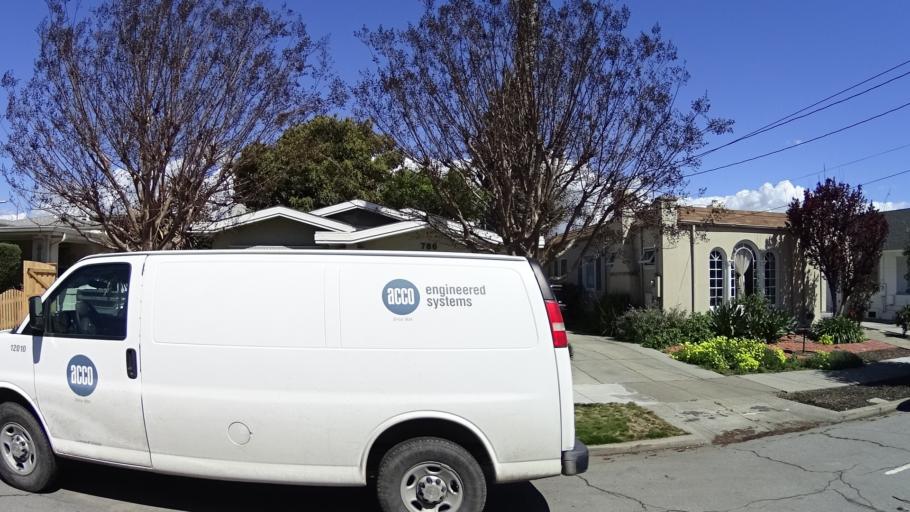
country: US
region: California
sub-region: Santa Clara County
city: San Jose
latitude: 37.3584
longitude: -121.8853
